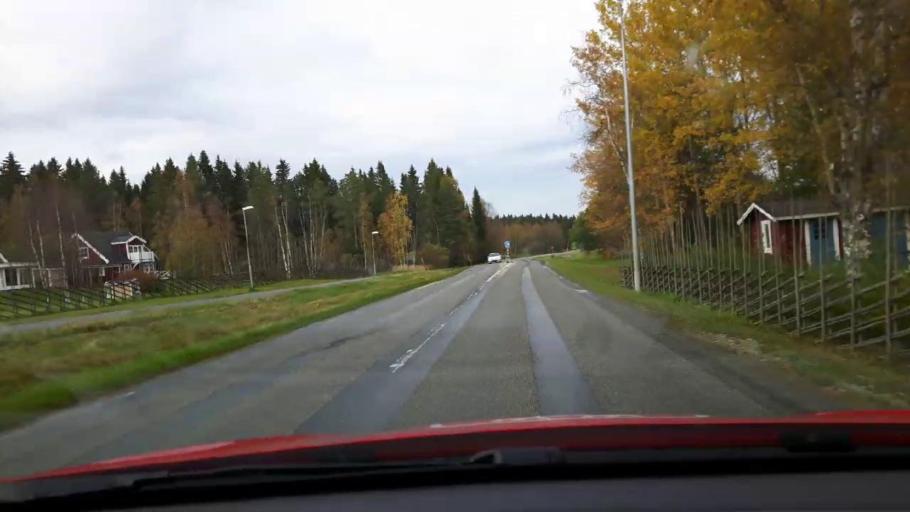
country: SE
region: Jaemtland
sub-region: Bergs Kommun
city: Hoverberg
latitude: 62.7778
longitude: 14.4309
